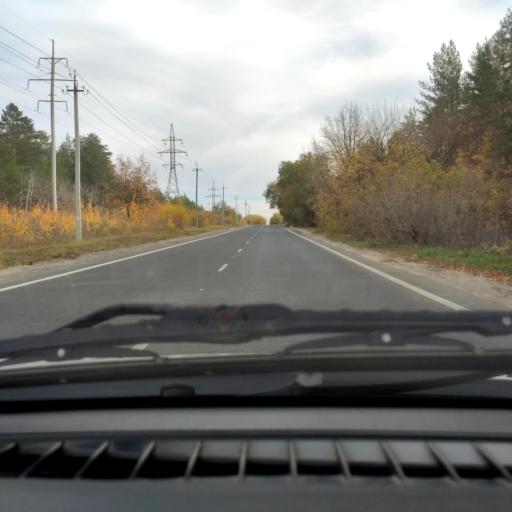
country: RU
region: Samara
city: Zhigulevsk
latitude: 53.5058
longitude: 49.4602
